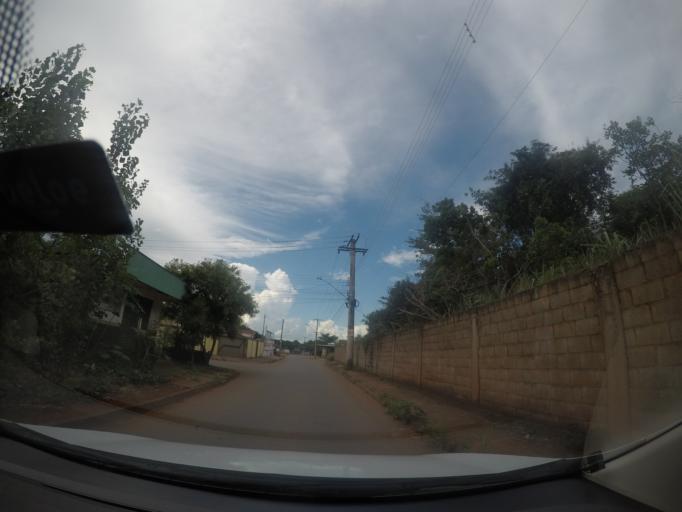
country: BR
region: Goias
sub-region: Goiania
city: Goiania
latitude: -16.7063
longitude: -49.3588
